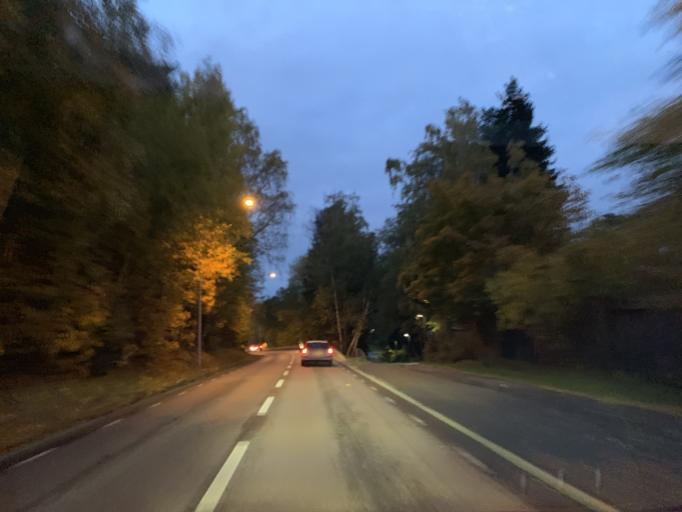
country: SE
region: Stockholm
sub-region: Botkyrka Kommun
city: Tumba
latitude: 59.1856
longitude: 17.8169
